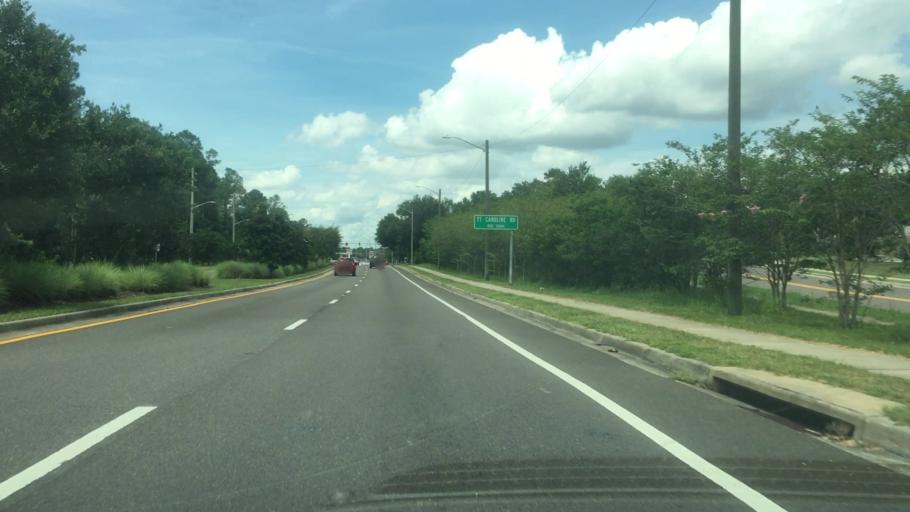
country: US
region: Florida
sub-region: Duval County
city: Jacksonville
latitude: 30.3580
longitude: -81.5497
